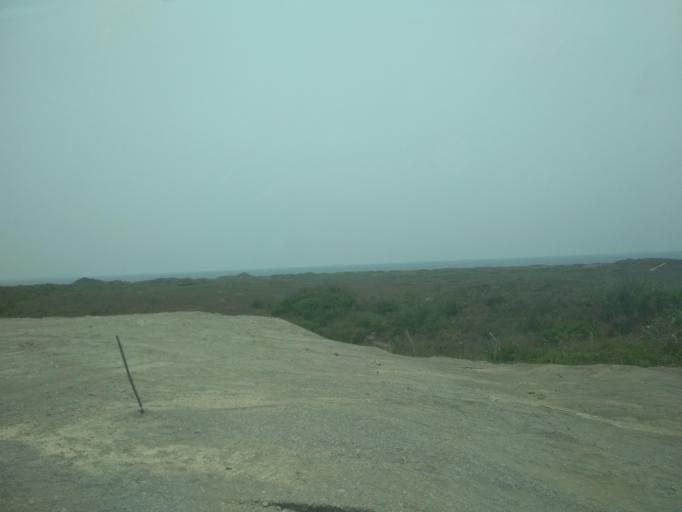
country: MX
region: Veracruz
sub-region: Alvarado
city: Playa de la Libertad
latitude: 19.0571
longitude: -96.0558
